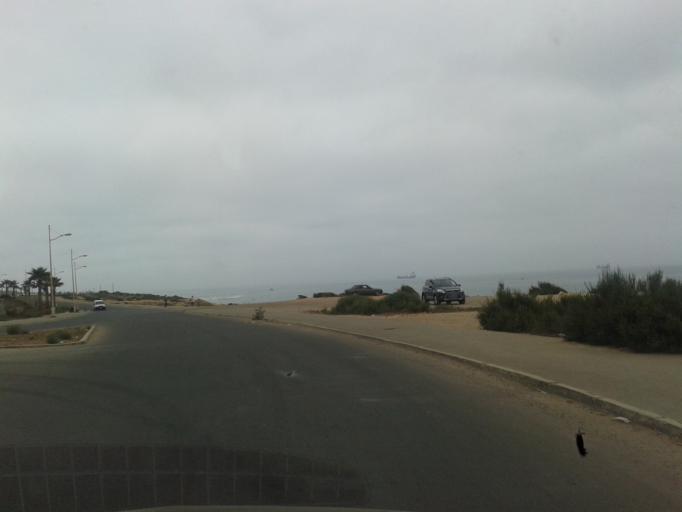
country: MA
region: Souss-Massa-Draa
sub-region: Agadir-Ida-ou-Tnan
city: Aourir
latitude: 30.4556
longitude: -9.6639
